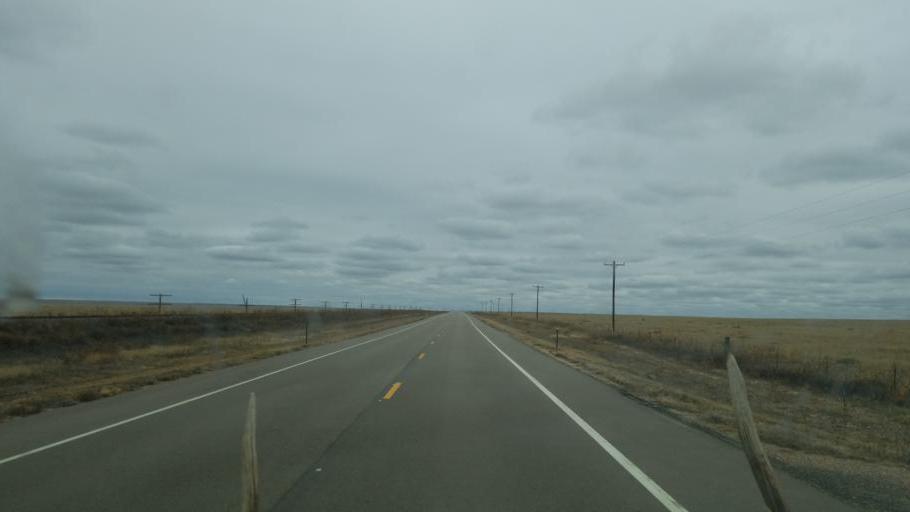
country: US
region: Colorado
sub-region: Bent County
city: Las Animas
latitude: 38.3993
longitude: -103.3018
